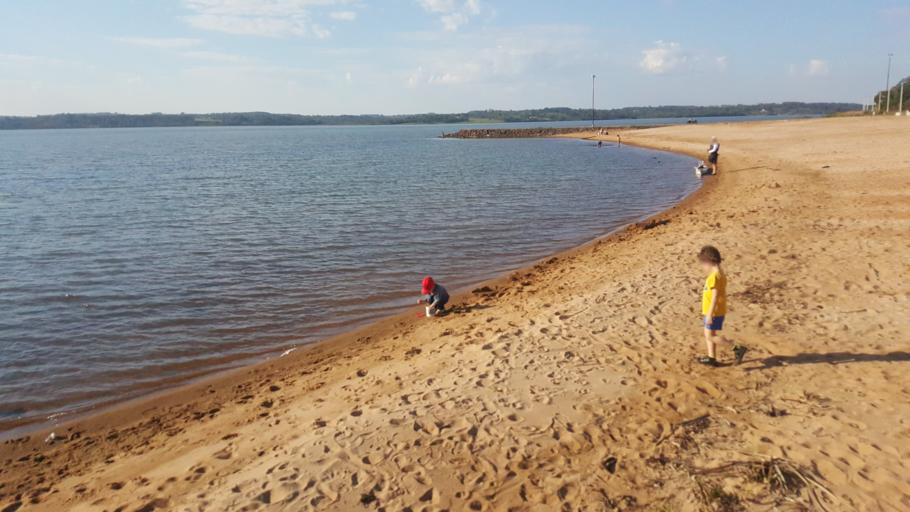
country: AR
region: Misiones
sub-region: Departamento de Candelaria
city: Candelaria
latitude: -27.4515
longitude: -55.7822
